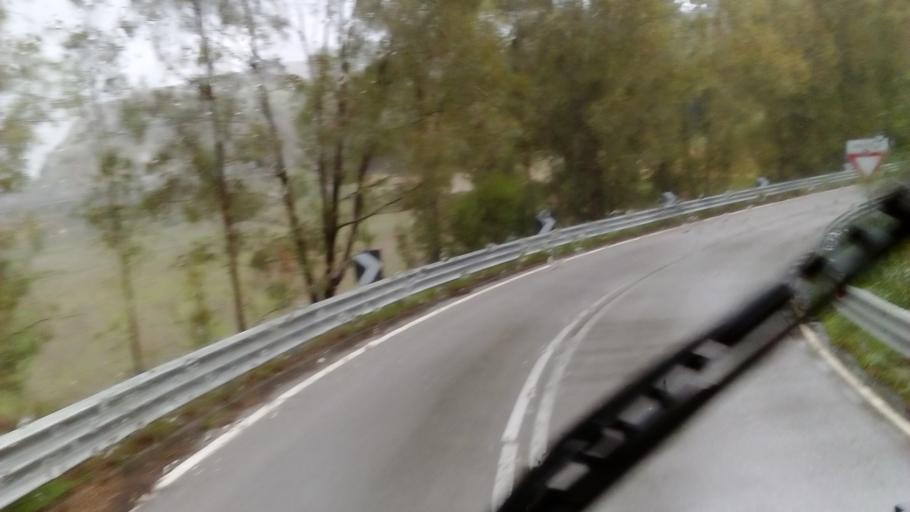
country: IT
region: Sicily
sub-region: Enna
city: Pietraperzia
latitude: 37.4918
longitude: 14.1484
